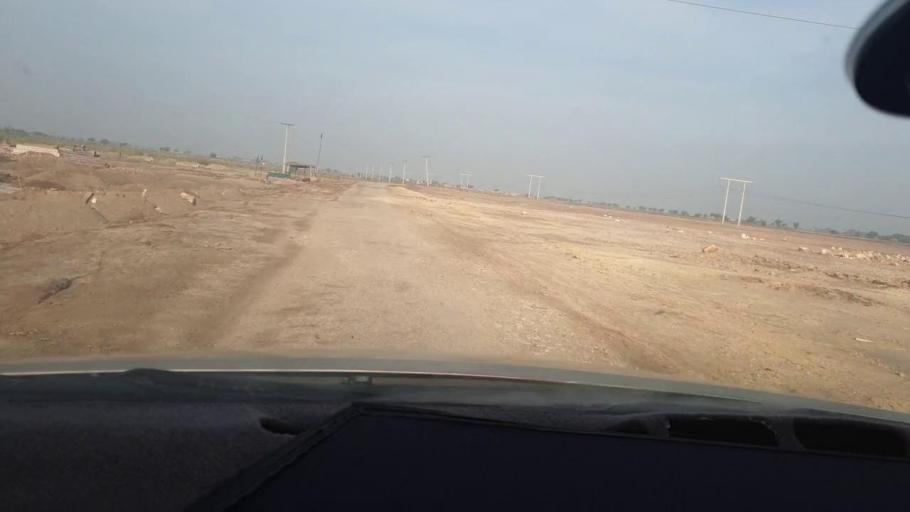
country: PK
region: Sindh
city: Jacobabad
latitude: 28.3344
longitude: 68.4148
